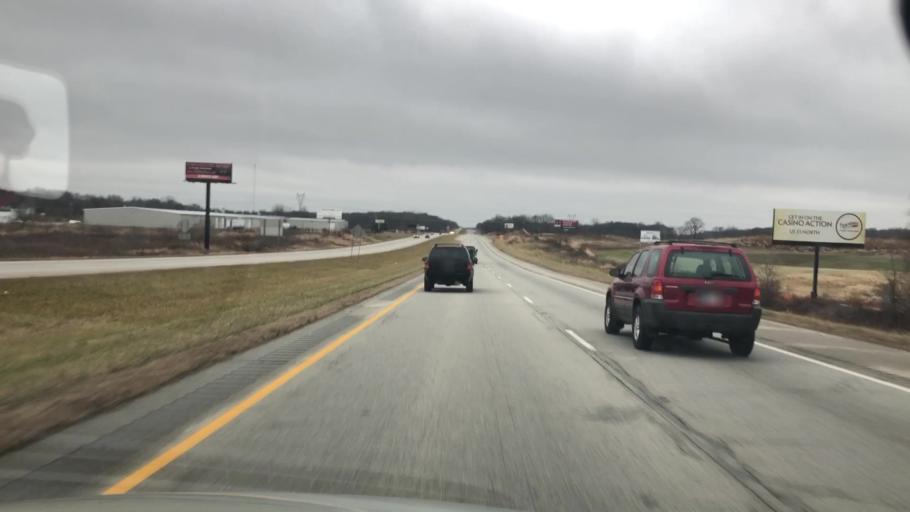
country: US
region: Indiana
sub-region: Kosciusko County
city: Warsaw
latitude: 41.2702
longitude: -85.8759
